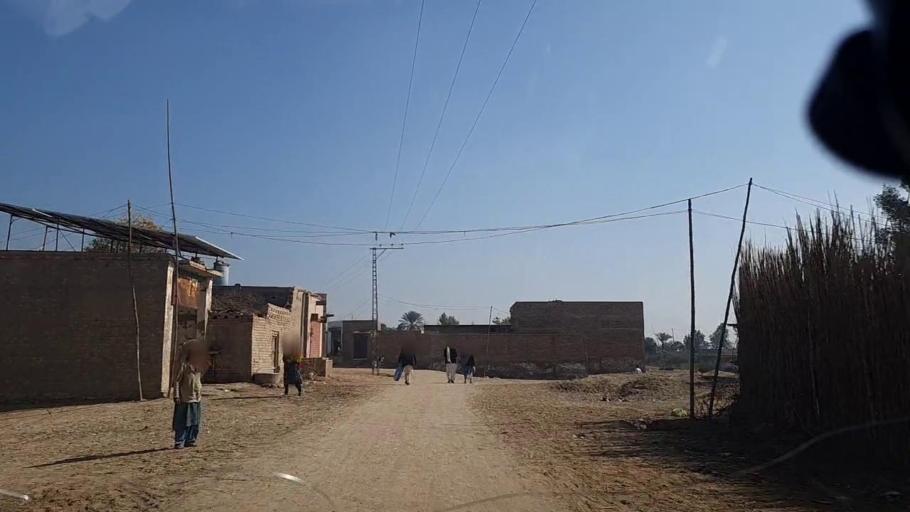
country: PK
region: Sindh
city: Khanpur
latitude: 27.8515
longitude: 69.4191
